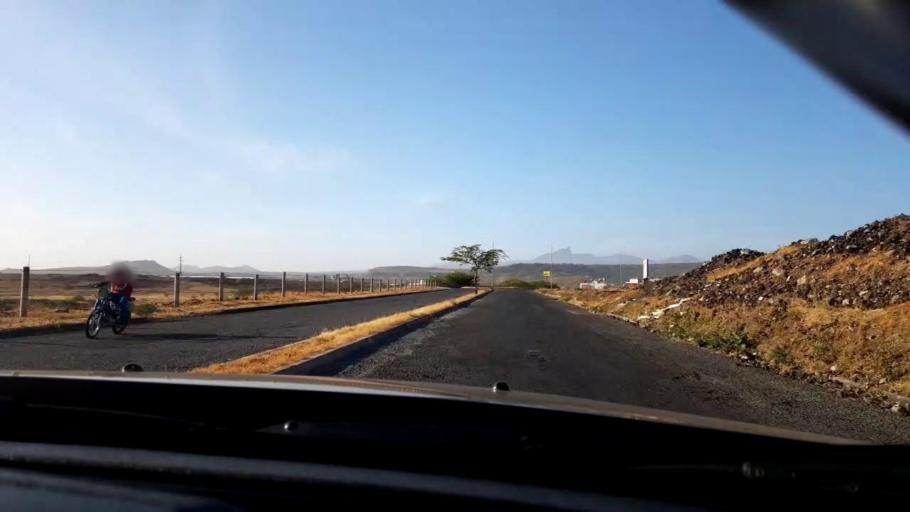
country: CV
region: Praia
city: Praia
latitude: 14.9145
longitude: -23.5405
